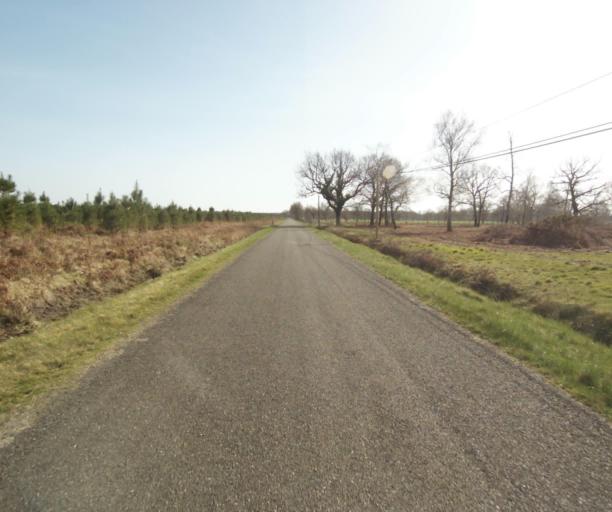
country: FR
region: Aquitaine
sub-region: Departement des Landes
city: Roquefort
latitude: 44.1405
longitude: -0.2638
